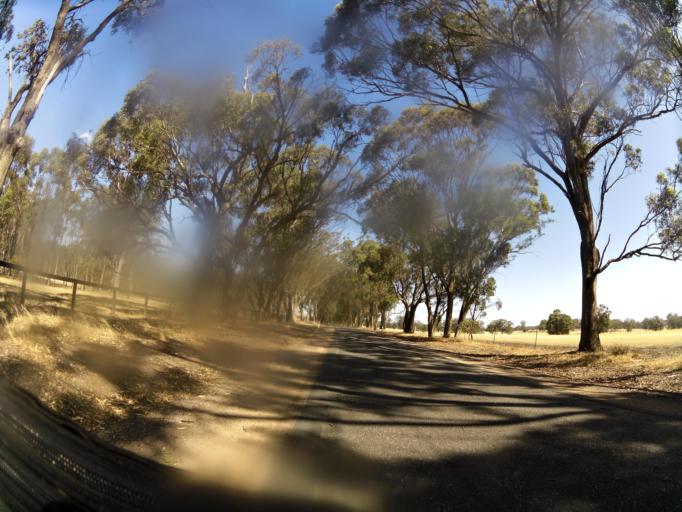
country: AU
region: Victoria
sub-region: Campaspe
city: Kyabram
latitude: -36.8875
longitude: 145.1011
